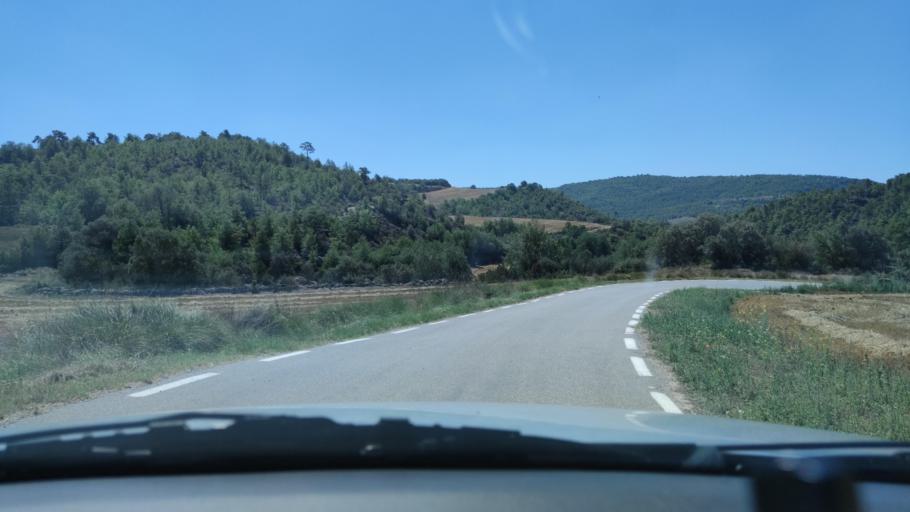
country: ES
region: Catalonia
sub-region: Provincia de Lleida
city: Tora de Riubregos
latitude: 41.8327
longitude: 1.4229
